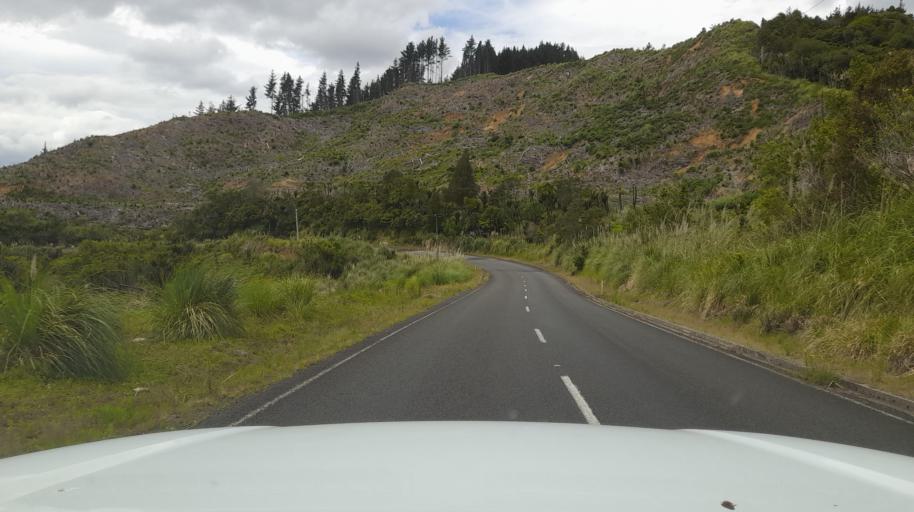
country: NZ
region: Northland
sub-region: Far North District
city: Kaitaia
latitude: -35.3717
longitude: 173.4312
